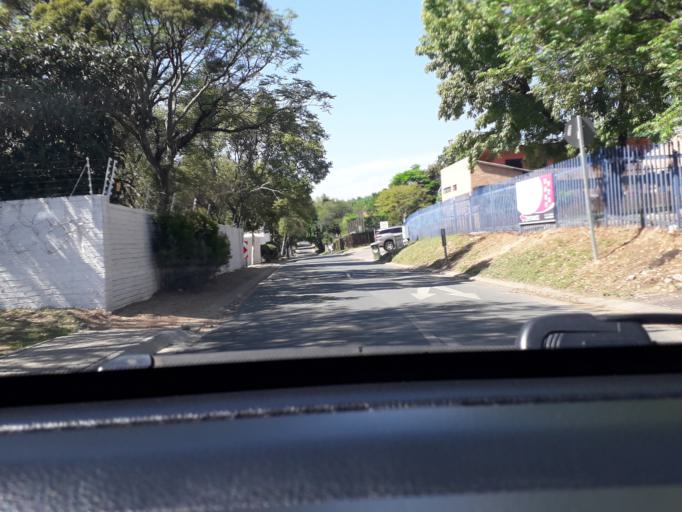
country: ZA
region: Gauteng
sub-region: City of Johannesburg Metropolitan Municipality
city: Midrand
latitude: -26.0586
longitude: 28.0634
